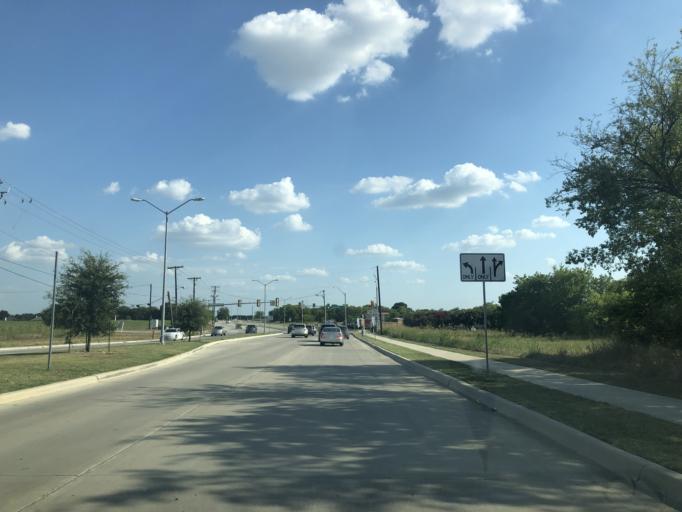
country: US
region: Texas
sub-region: Tarrant County
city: Saginaw
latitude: 32.8598
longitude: -97.3909
